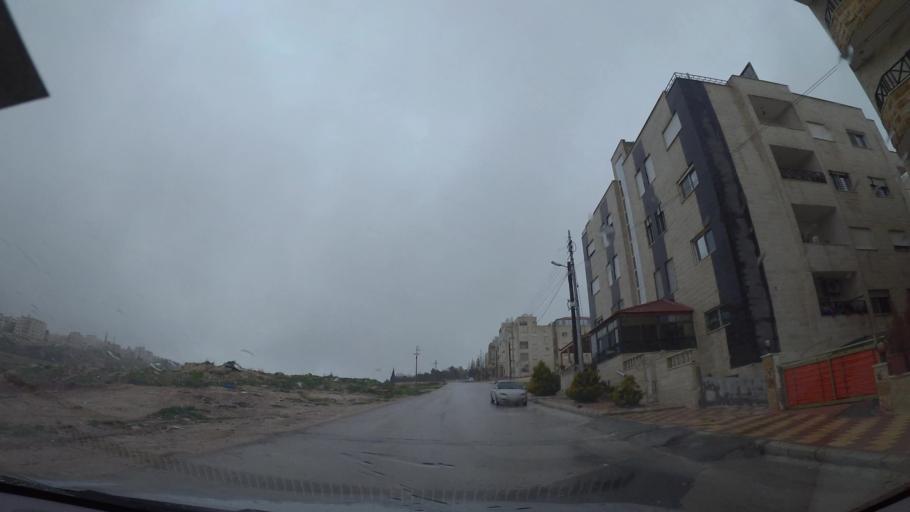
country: JO
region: Amman
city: Al Jubayhah
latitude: 32.0452
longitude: 35.8776
